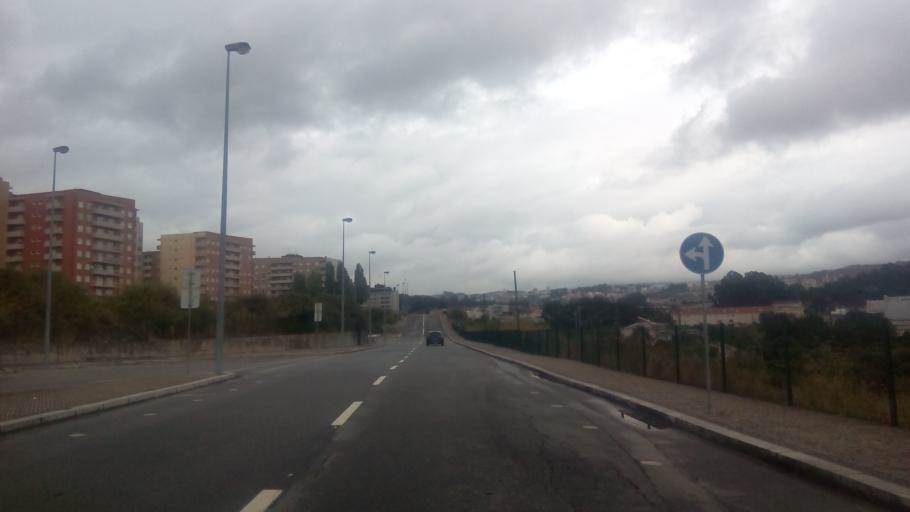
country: PT
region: Porto
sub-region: Paredes
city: Casteloes de Cepeda
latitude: 41.2011
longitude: -8.3327
